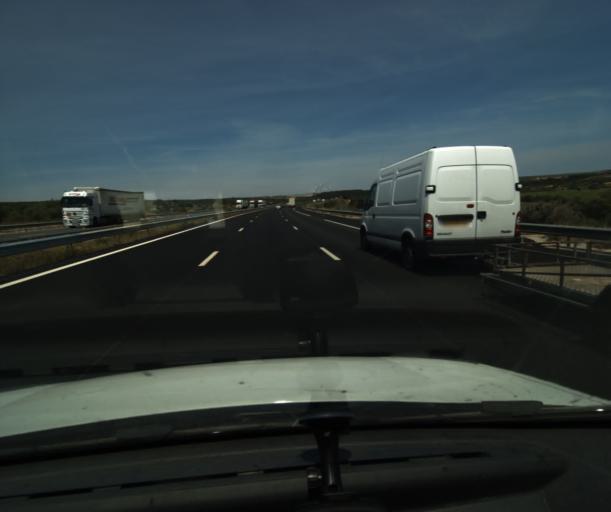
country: FR
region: Languedoc-Roussillon
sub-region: Departement de l'Aude
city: Sigean
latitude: 42.9686
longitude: 2.9692
